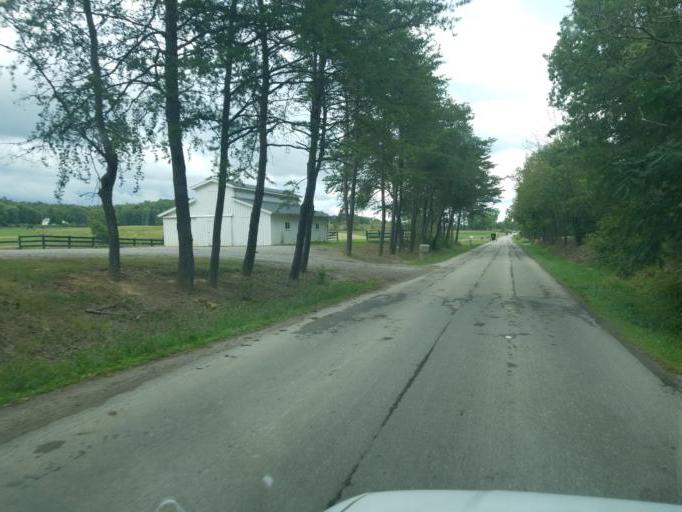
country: US
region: Ohio
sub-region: Jackson County
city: Oak Hill
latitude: 38.9412
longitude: -82.5984
